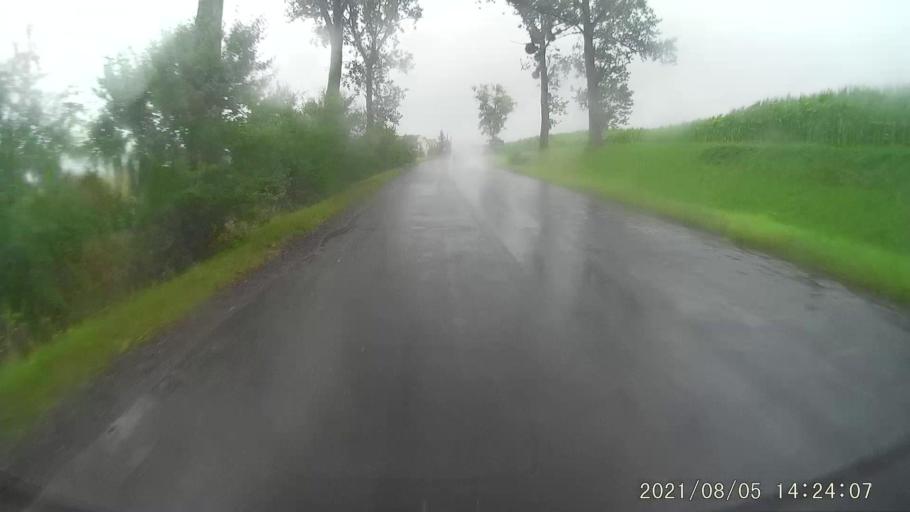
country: PL
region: Opole Voivodeship
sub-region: Powiat nyski
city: Korfantow
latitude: 50.4826
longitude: 17.6398
